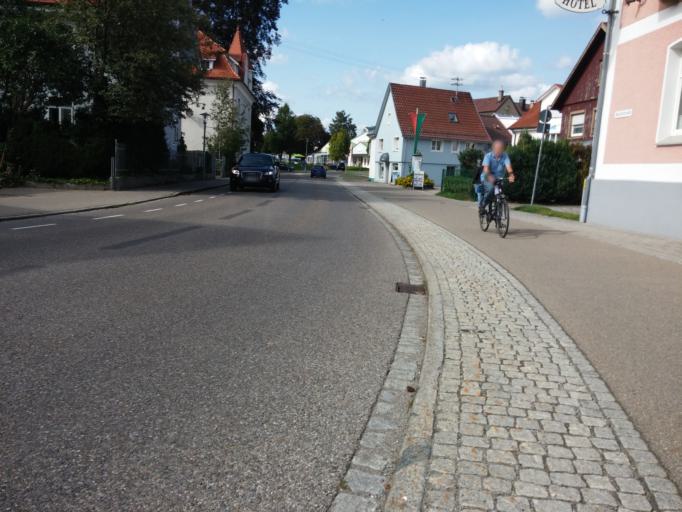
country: DE
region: Baden-Wuerttemberg
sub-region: Tuebingen Region
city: Isny im Allgau
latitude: 47.6966
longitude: 10.0430
